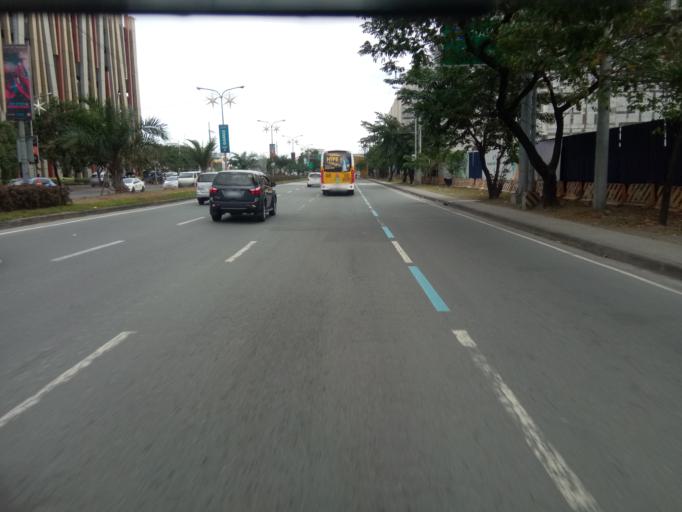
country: PH
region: Metro Manila
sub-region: Makati City
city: Makati City
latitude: 14.5246
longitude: 120.9903
